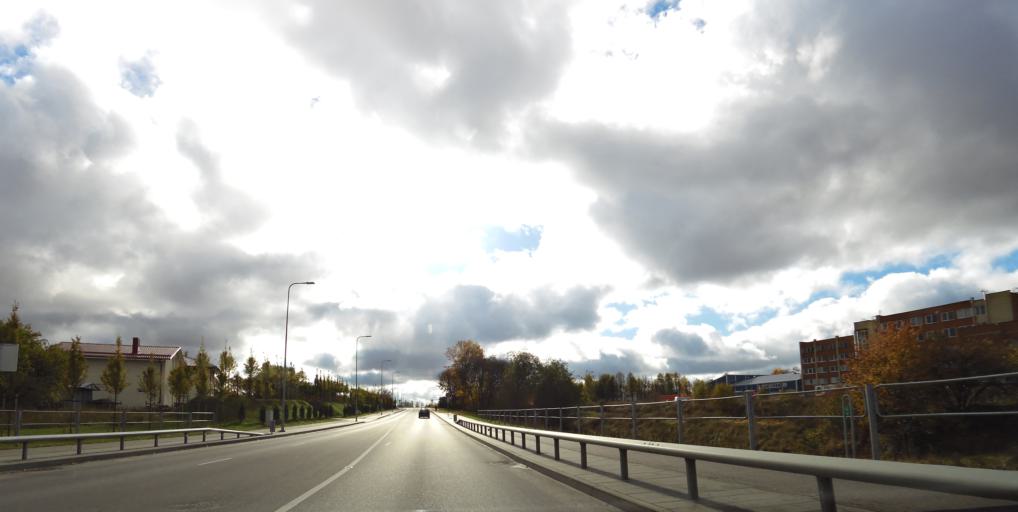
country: LT
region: Vilnius County
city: Naujamiestis
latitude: 54.6495
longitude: 25.2763
